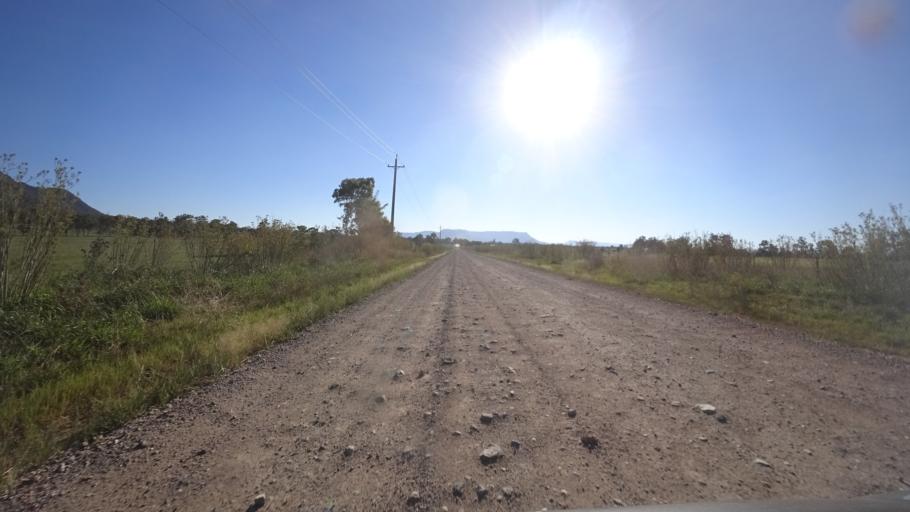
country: AU
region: New South Wales
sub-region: Lithgow
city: Portland
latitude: -33.1011
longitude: 150.2275
